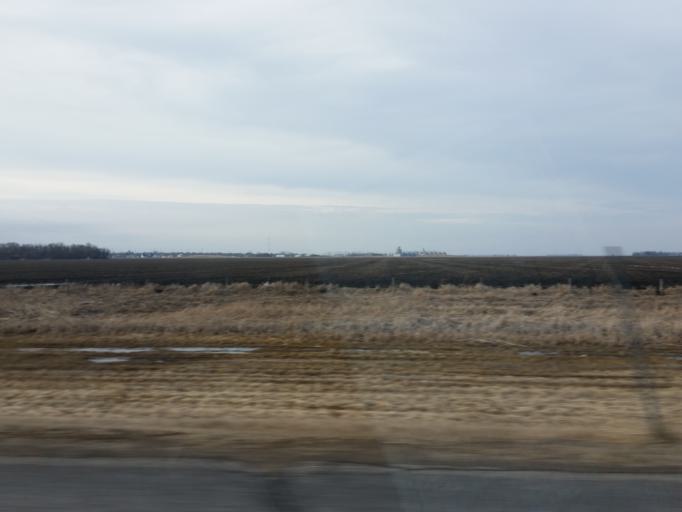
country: US
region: North Dakota
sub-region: Cass County
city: Casselton
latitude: 46.8768
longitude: -97.1924
